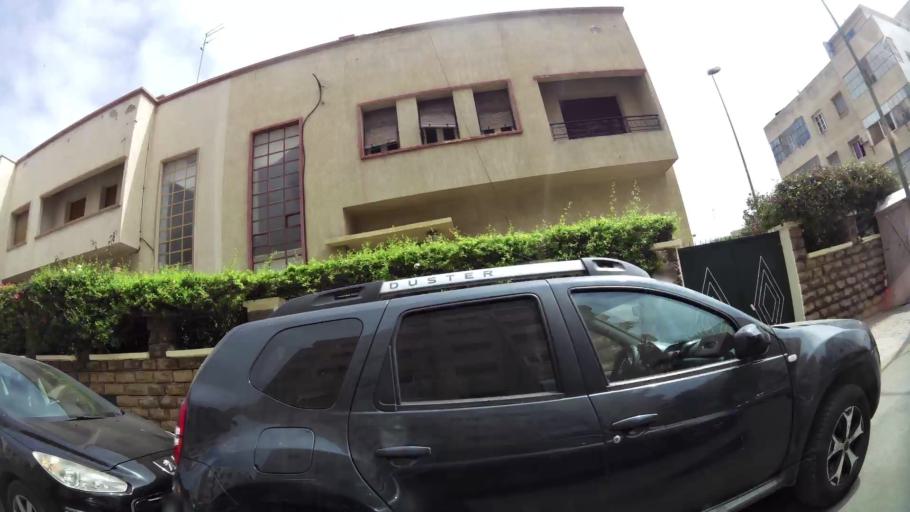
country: MA
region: Rabat-Sale-Zemmour-Zaer
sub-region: Rabat
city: Rabat
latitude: 34.0159
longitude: -6.8473
